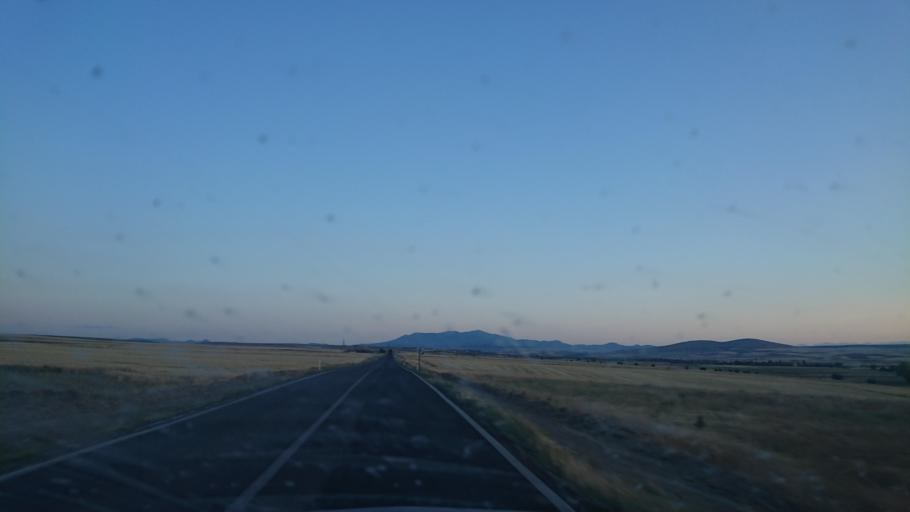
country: TR
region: Aksaray
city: Balci
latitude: 38.8319
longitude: 34.1388
